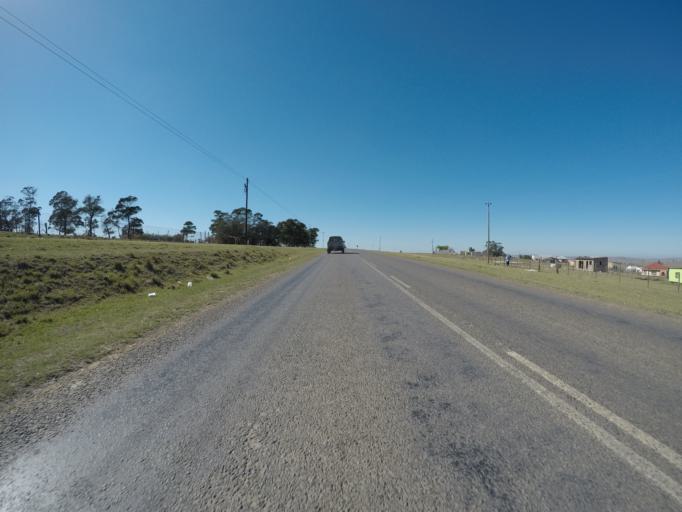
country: ZA
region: Eastern Cape
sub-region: OR Tambo District Municipality
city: Mthatha
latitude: -31.7896
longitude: 28.7442
